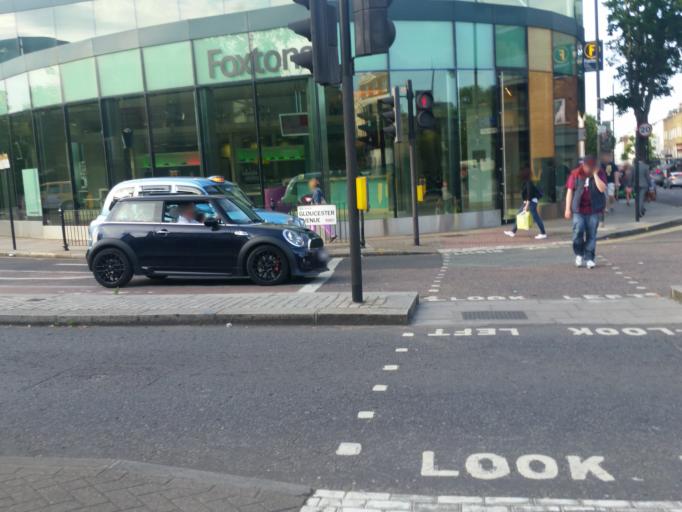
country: GB
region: England
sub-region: Greater London
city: Camden Town
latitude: 51.5368
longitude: -0.1464
